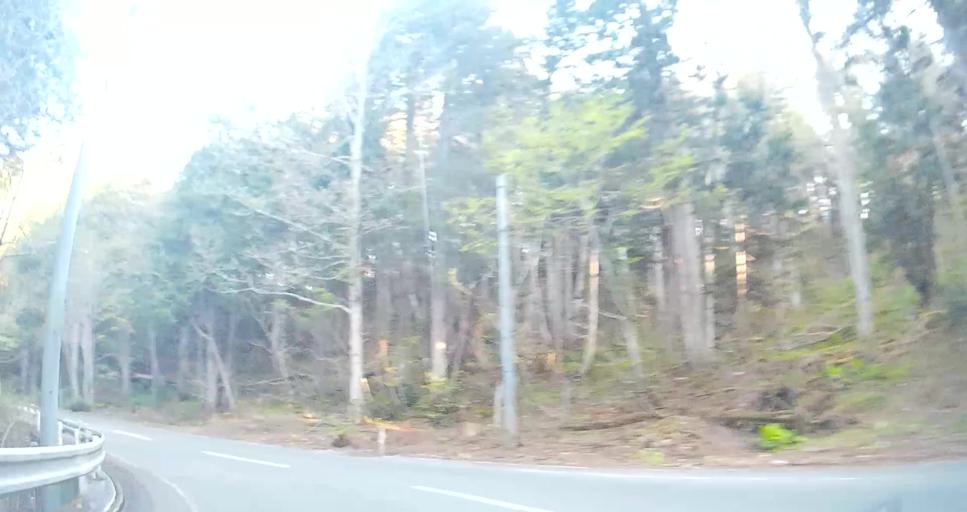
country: JP
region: Aomori
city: Mutsu
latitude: 41.3180
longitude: 141.1318
